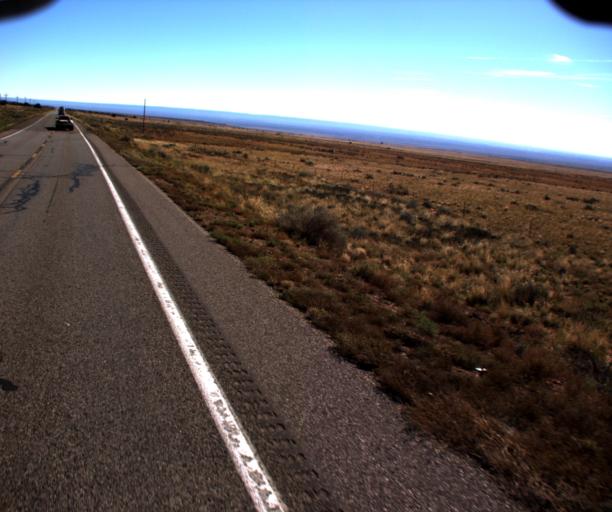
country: US
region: Arizona
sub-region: Mohave County
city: Colorado City
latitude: 36.8584
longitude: -112.8047
